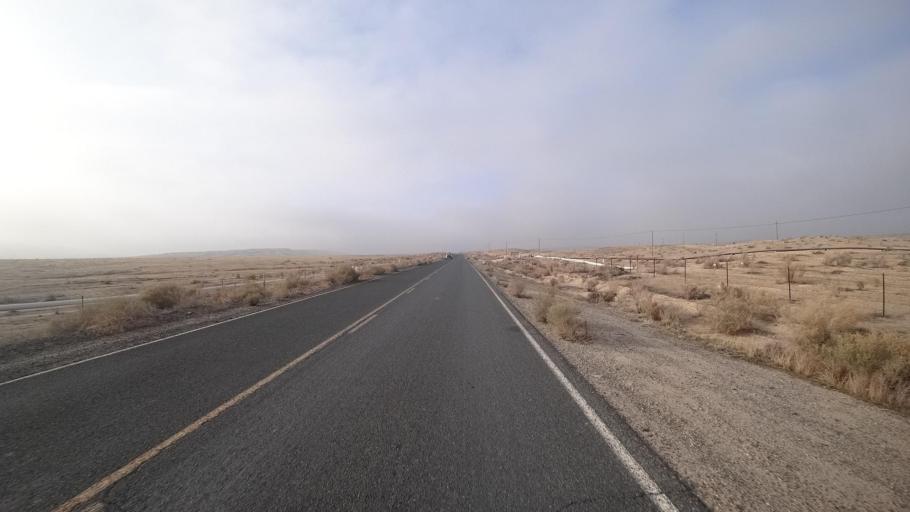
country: US
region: California
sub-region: Kern County
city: Ford City
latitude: 35.2379
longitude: -119.4481
